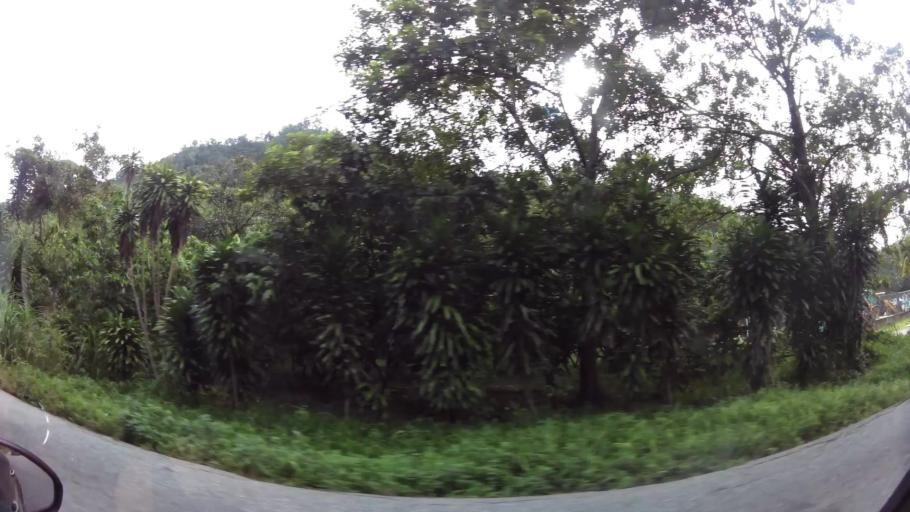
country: TT
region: San Juan/Laventille
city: Laventille
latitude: 10.6861
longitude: -61.4582
